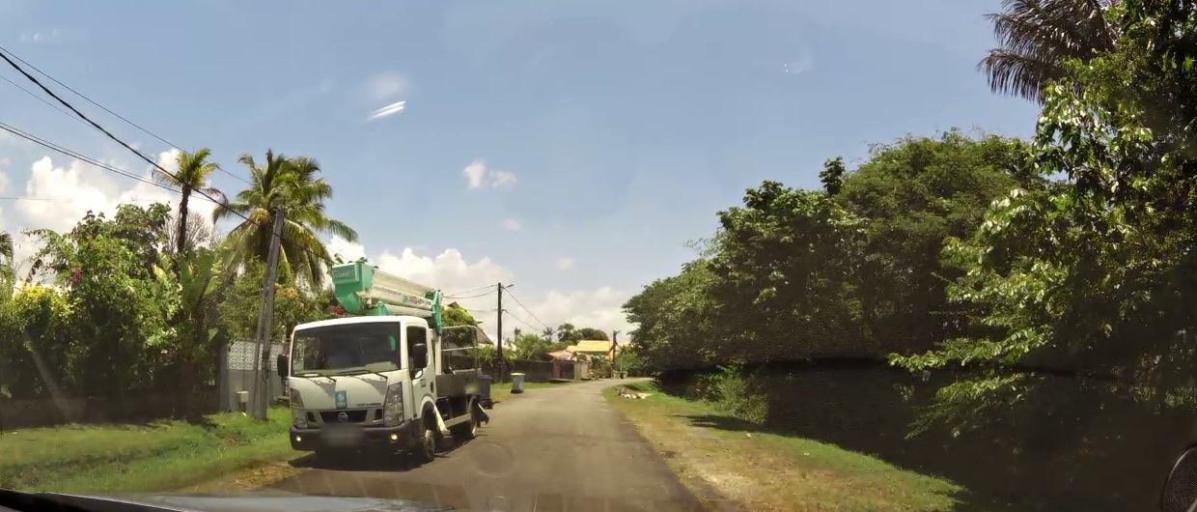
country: GF
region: Guyane
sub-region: Guyane
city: Cayenne
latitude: 4.9361
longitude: -52.3044
